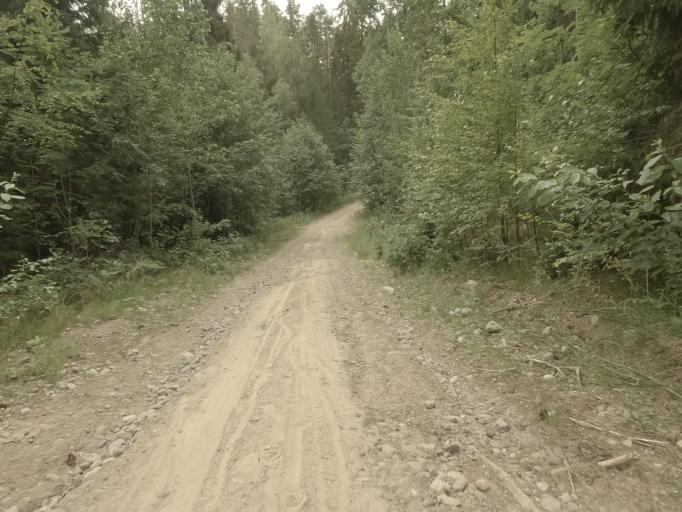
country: RU
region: Leningrad
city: Kamennogorsk
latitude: 61.0705
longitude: 29.1662
